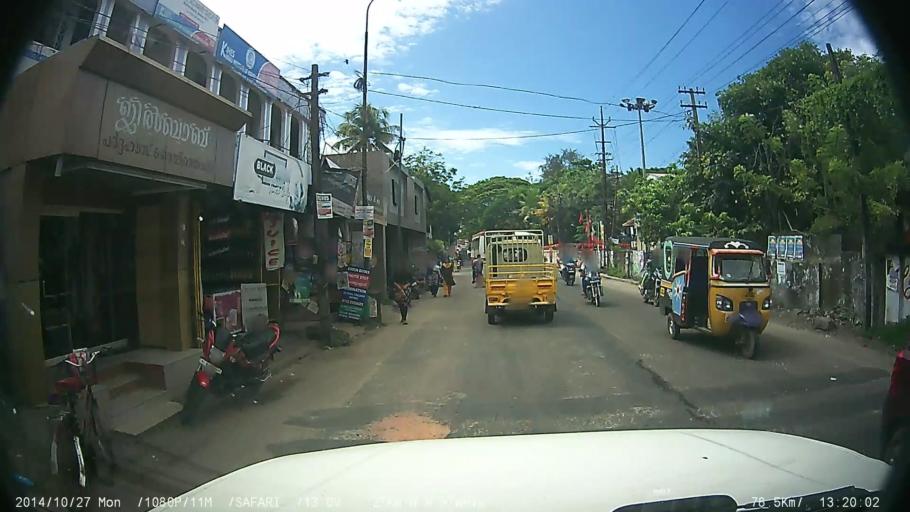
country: IN
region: Kerala
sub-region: Alappuzha
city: Alleppey
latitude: 9.4922
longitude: 76.3297
